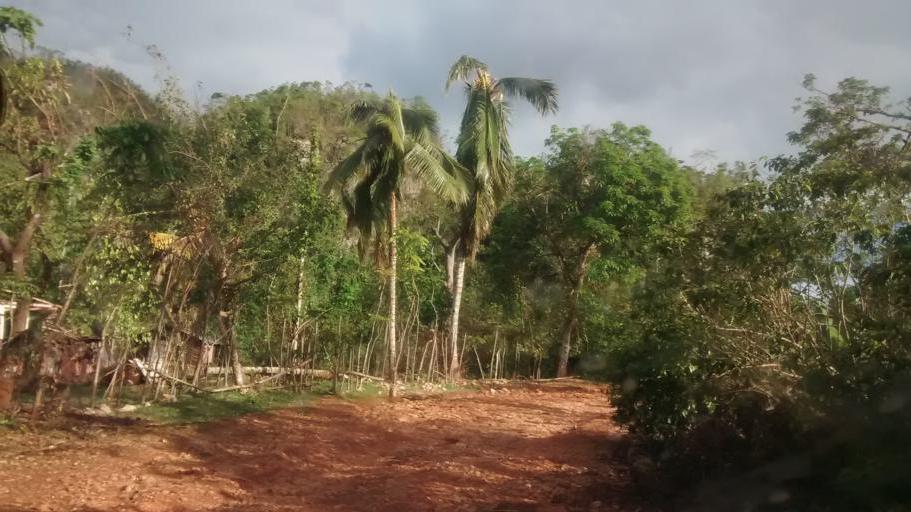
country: HT
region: Grandans
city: Corail
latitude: 18.5157
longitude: -73.7851
